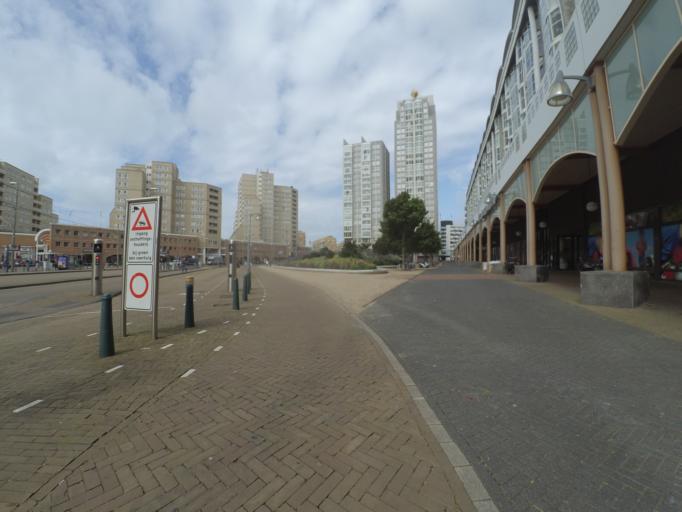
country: NL
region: South Holland
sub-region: Gemeente Den Haag
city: Scheveningen
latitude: 52.1130
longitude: 4.2841
